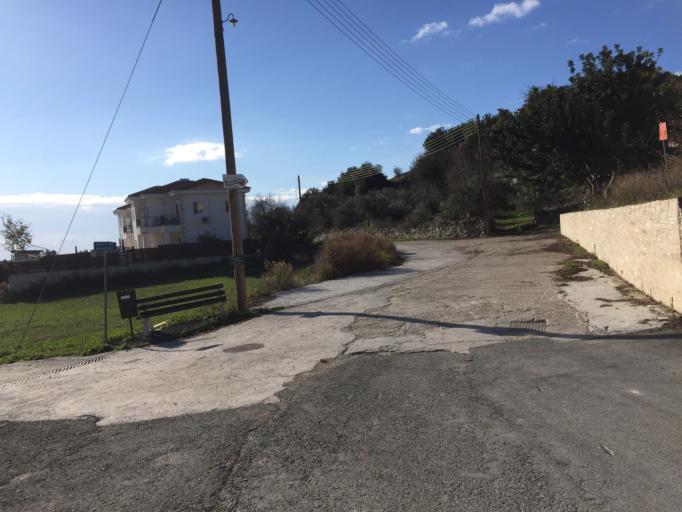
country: CY
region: Pafos
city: Mesogi
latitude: 34.8449
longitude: 32.5032
